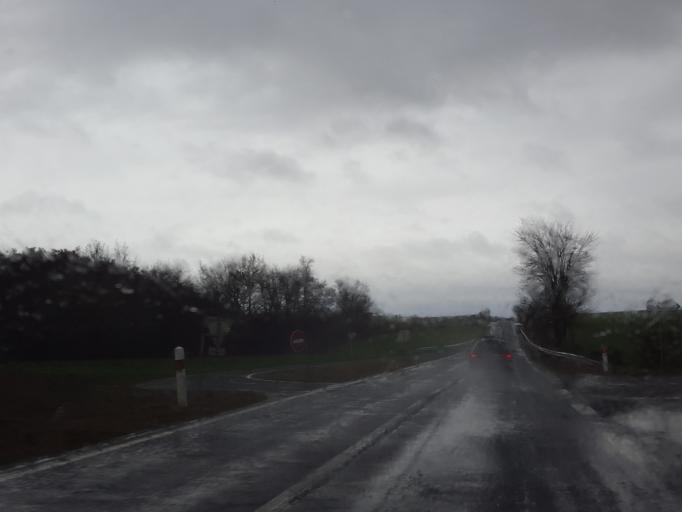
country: FR
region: Languedoc-Roussillon
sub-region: Departement de l'Aude
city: Saint-Martin-Lalande
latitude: 43.1648
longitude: 1.9941
